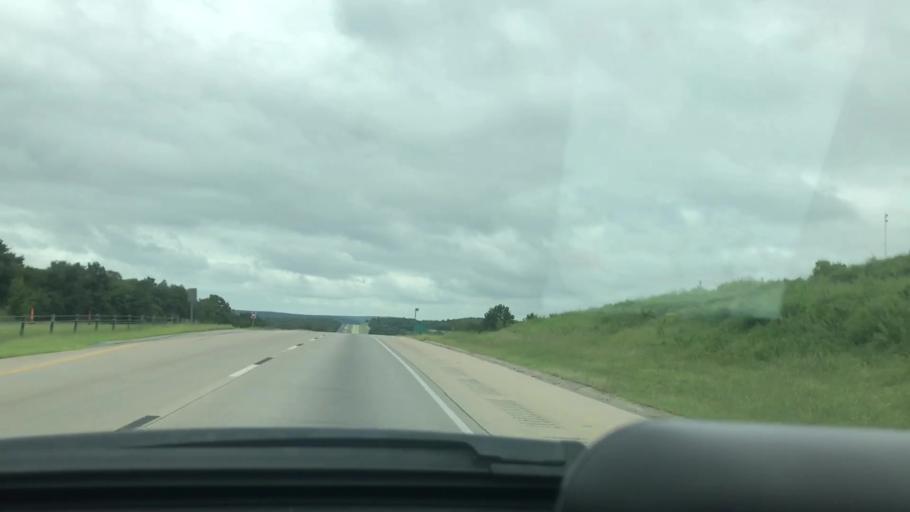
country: US
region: Oklahoma
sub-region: Pittsburg County
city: Krebs
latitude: 34.9702
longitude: -95.7237
